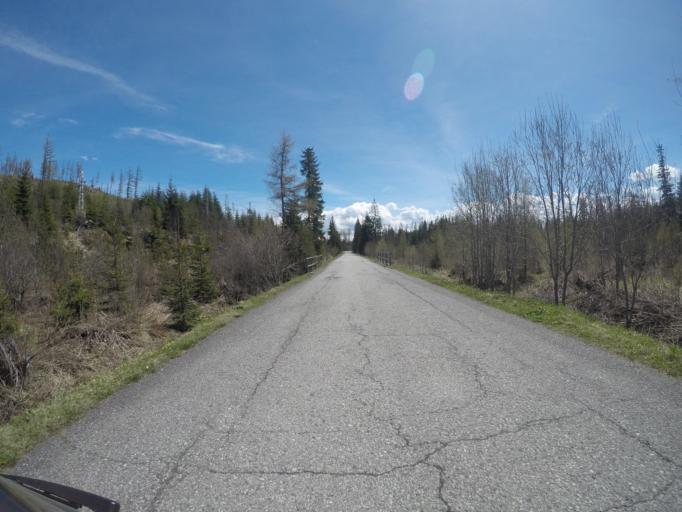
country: SK
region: Presovsky
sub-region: Okres Poprad
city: Strba
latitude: 49.1185
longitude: 20.0779
